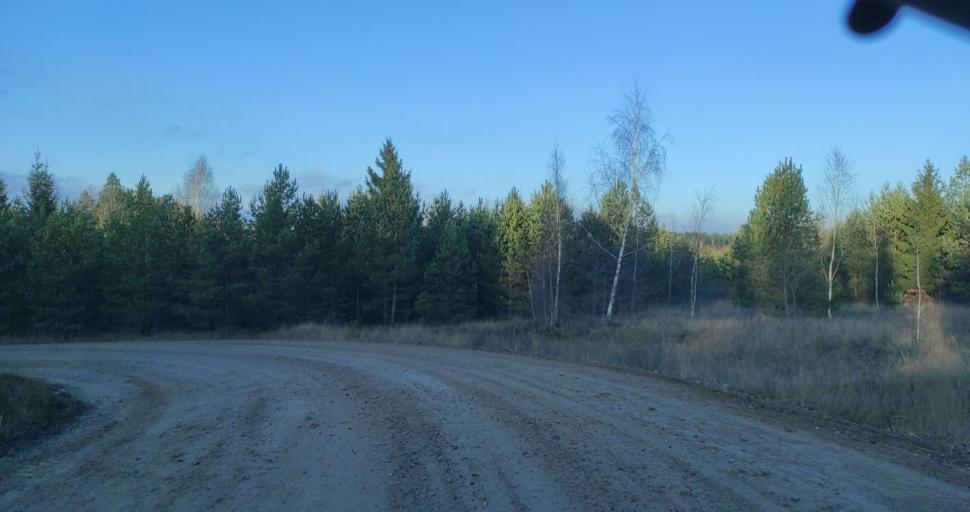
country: LV
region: Kuldigas Rajons
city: Kuldiga
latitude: 57.0583
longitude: 21.8655
